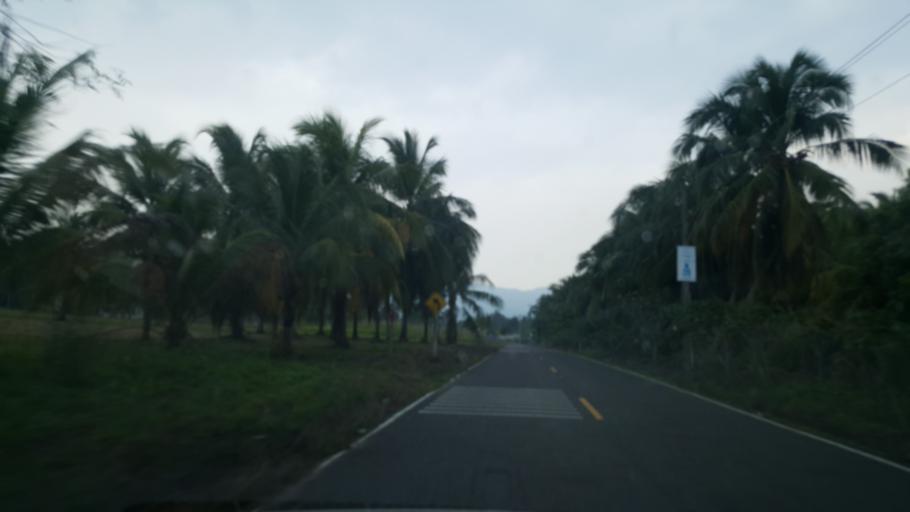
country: TH
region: Chon Buri
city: Ban Bueng
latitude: 13.2298
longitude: 101.0350
